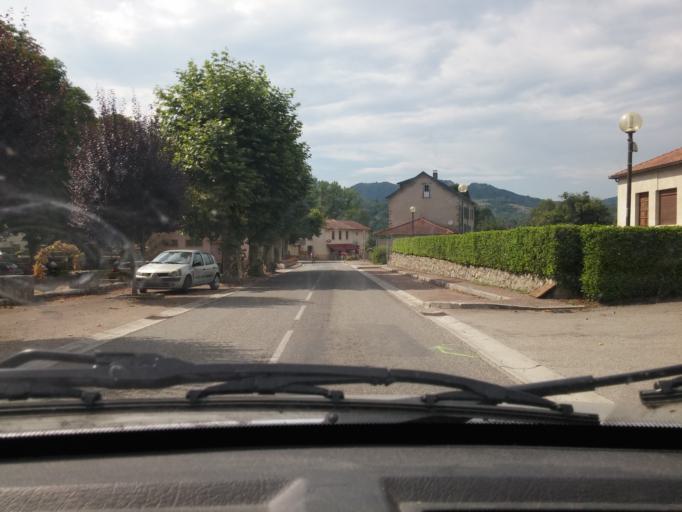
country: FR
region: Midi-Pyrenees
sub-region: Departement de l'Ariege
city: Saint-Girons
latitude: 42.8741
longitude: 1.2186
